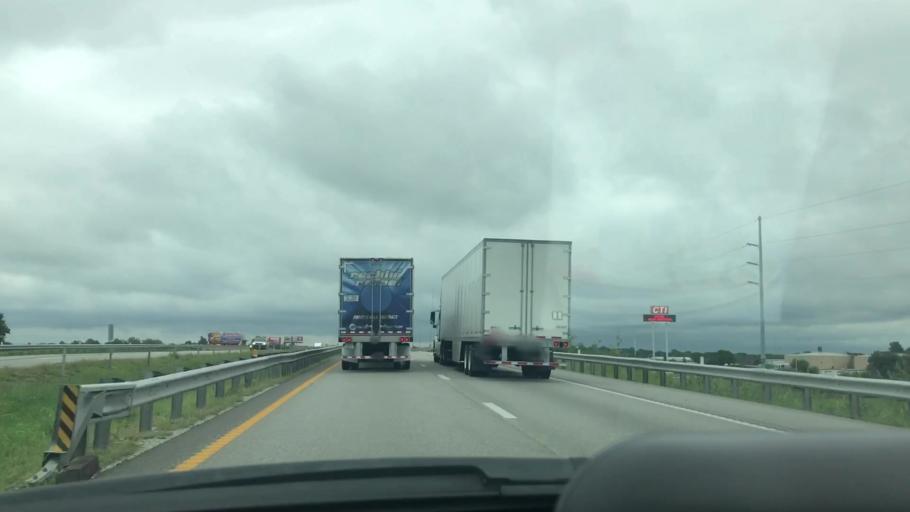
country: US
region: Missouri
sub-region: Greene County
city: Springfield
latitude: 37.2196
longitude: -93.3773
